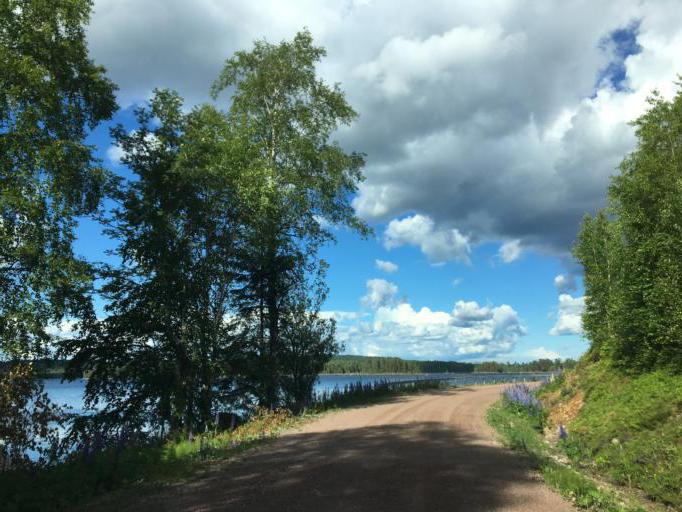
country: SE
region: OErebro
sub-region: Hallefors Kommun
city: Haellefors
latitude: 60.0455
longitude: 14.4595
